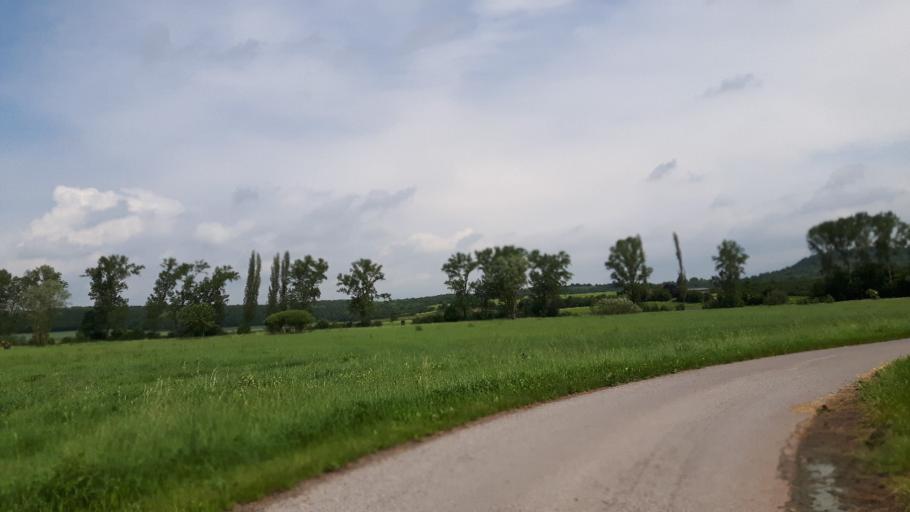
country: DE
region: Bavaria
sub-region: Regierungsbezirk Unterfranken
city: Bad Konigshofen im Grabfeld
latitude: 50.3040
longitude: 10.4980
